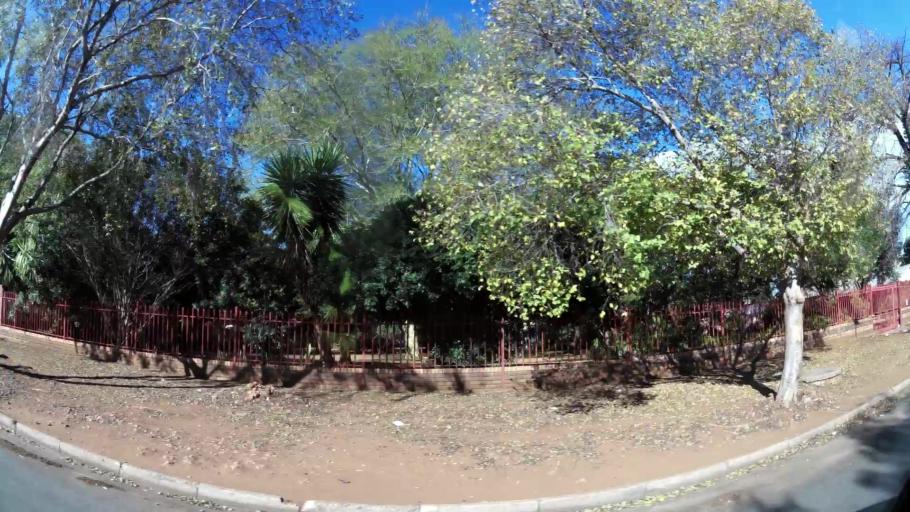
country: ZA
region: Limpopo
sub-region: Waterberg District Municipality
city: Mokopane
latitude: -24.1787
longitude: 29.0014
